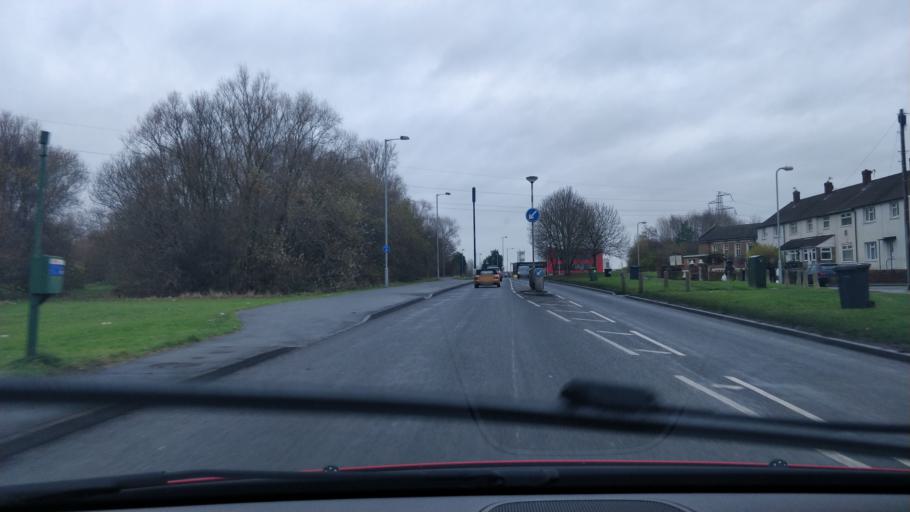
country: GB
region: England
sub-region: Sefton
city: Thornton
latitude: 53.4885
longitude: -2.9906
